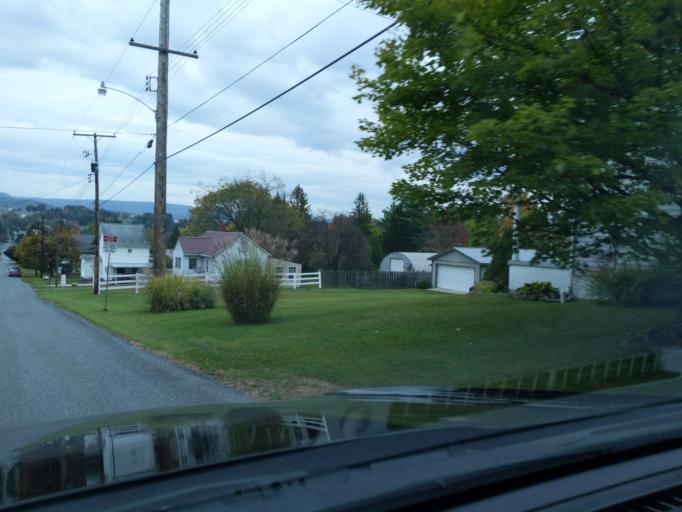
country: US
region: Pennsylvania
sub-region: Blair County
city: Altoona
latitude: 40.5027
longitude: -78.3786
